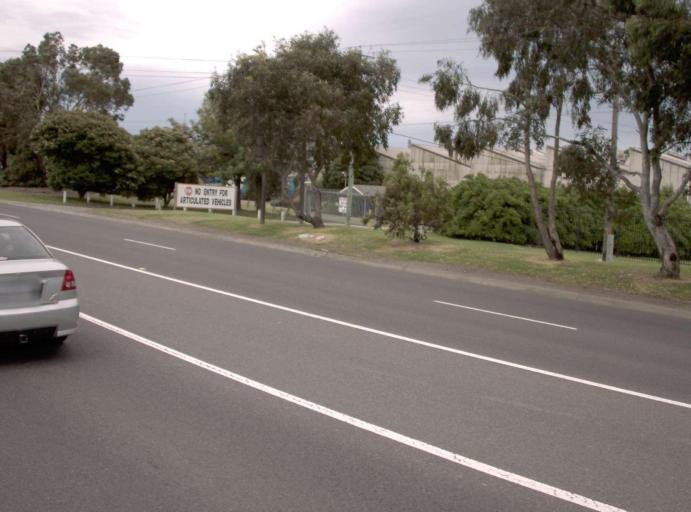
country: AU
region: Victoria
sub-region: Casey
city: Doveton
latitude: -38.0084
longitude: 145.2292
